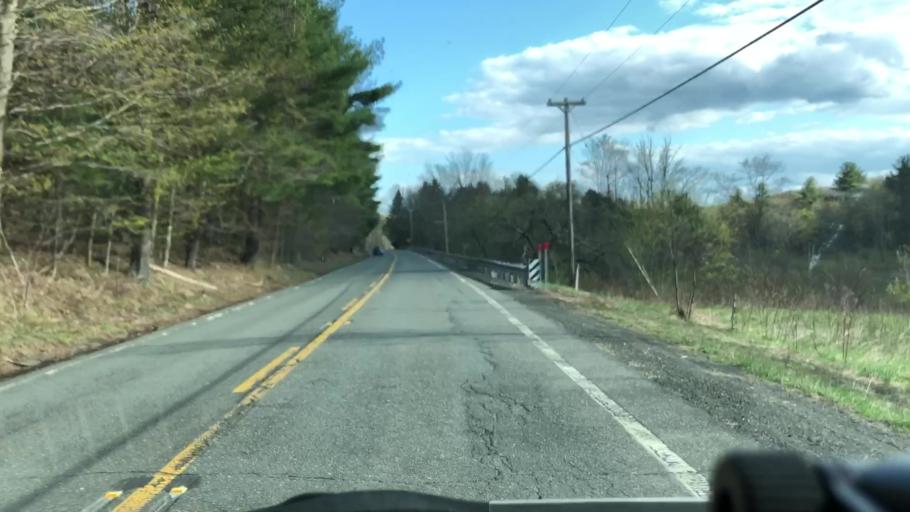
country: US
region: Massachusetts
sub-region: Hampshire County
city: Chesterfield
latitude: 42.3580
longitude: -72.9064
